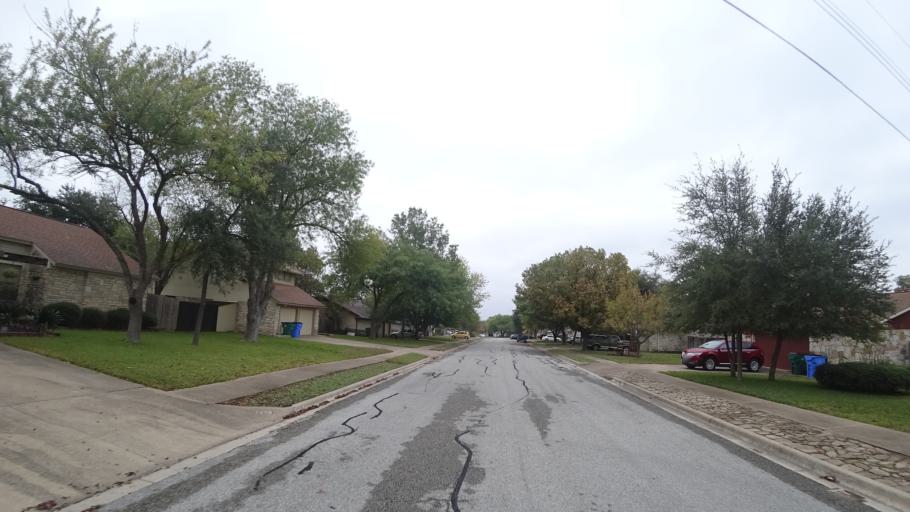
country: US
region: Texas
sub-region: Travis County
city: Pflugerville
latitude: 30.4269
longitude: -97.6116
